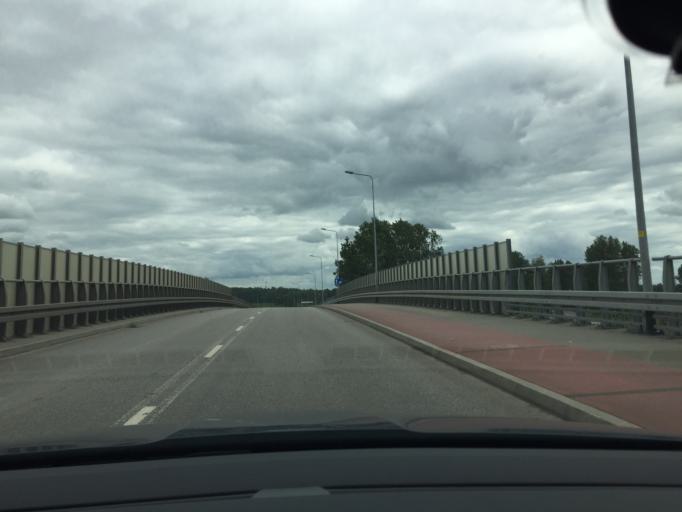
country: PL
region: Pomeranian Voivodeship
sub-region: Gdansk
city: Gdansk
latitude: 54.3768
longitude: 18.6802
